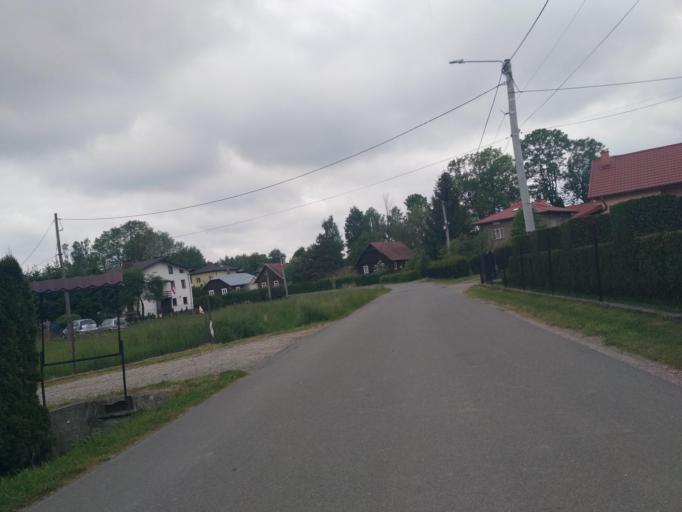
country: PL
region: Subcarpathian Voivodeship
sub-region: Powiat krosnienski
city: Chorkowka
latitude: 49.6678
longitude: 21.7066
